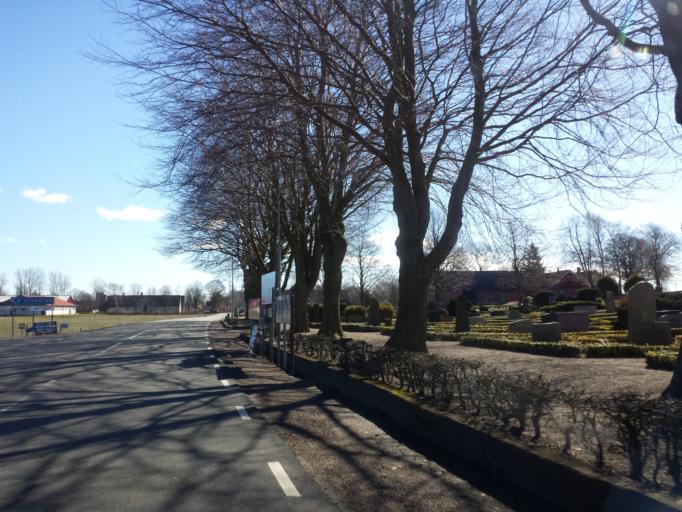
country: SE
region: Skane
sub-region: Tomelilla Kommun
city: Tomelilla
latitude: 55.6229
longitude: 13.8508
